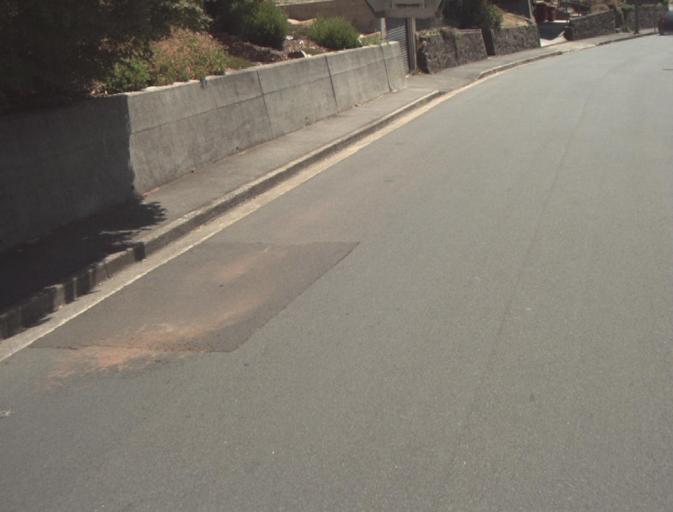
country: AU
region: Tasmania
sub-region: Launceston
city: West Launceston
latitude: -41.4566
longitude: 147.1316
